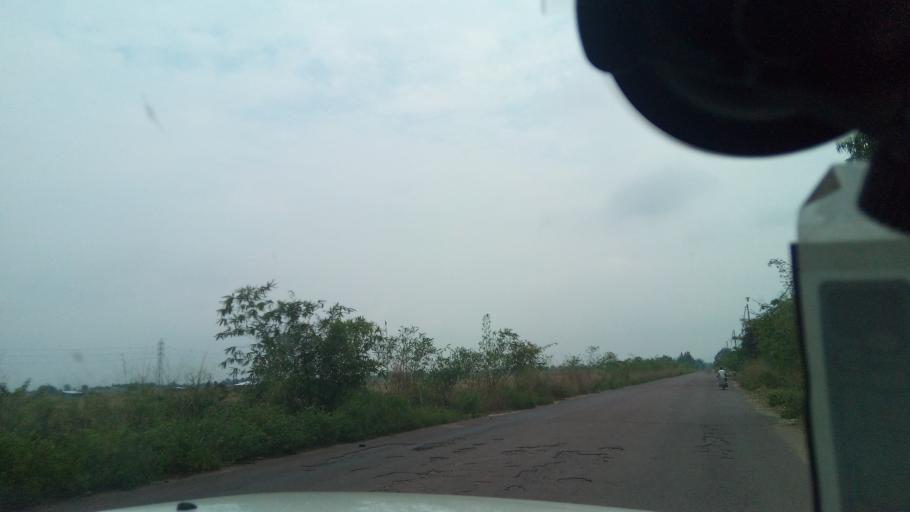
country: CD
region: Kinshasa
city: Masina
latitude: -4.2011
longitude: 15.5635
